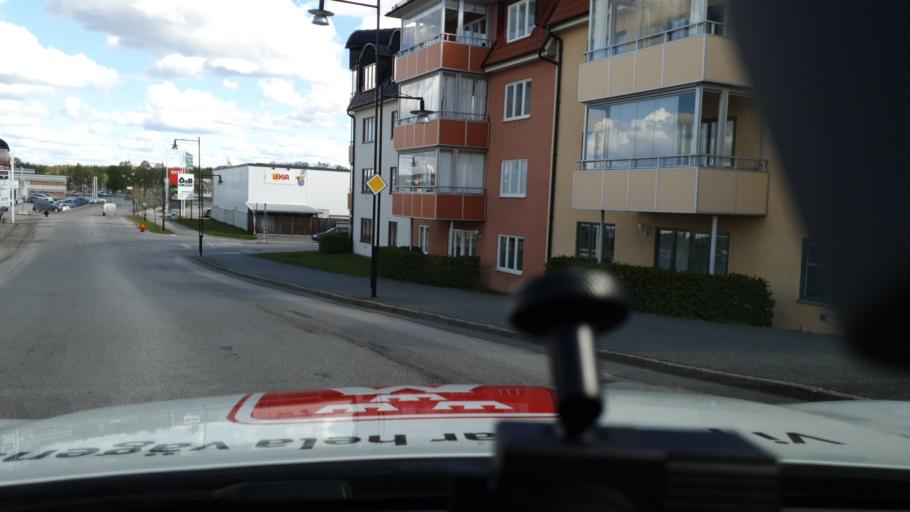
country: SE
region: Kalmar
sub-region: Vimmerby Kommun
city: Vimmerby
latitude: 57.6666
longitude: 15.8470
